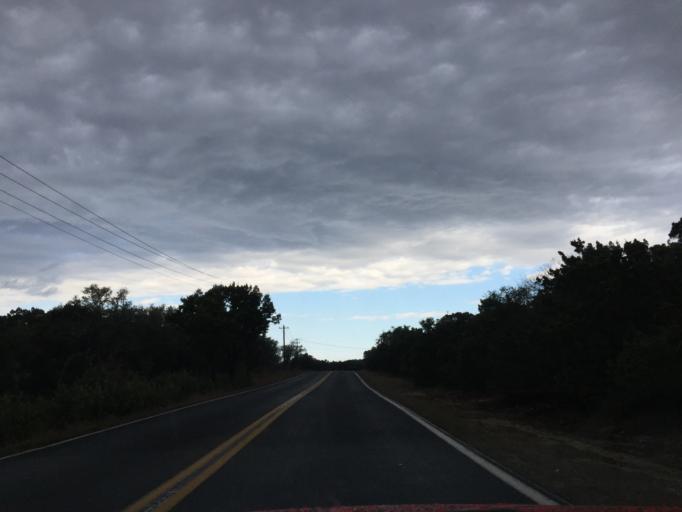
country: US
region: Texas
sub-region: Williamson County
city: Leander
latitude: 30.6131
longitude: -97.9393
